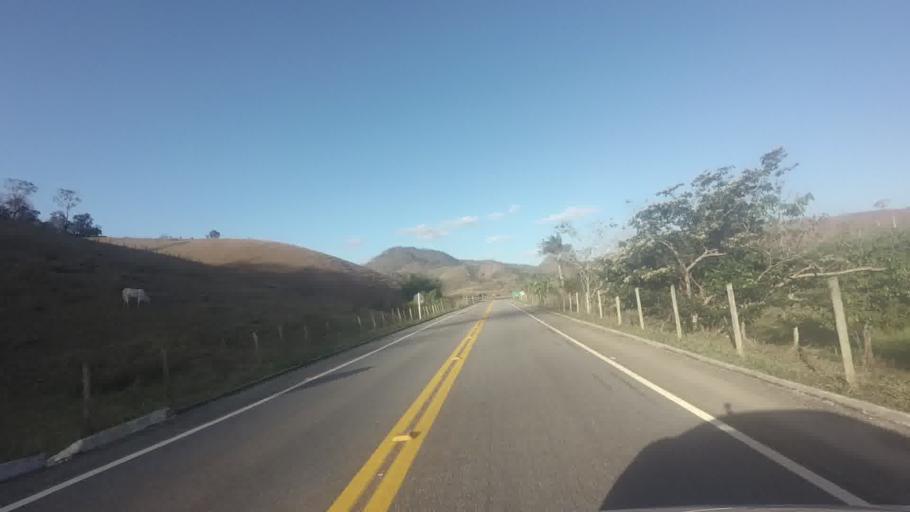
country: BR
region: Espirito Santo
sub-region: Jeronimo Monteiro
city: Jeronimo Monteiro
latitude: -20.8860
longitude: -41.2742
